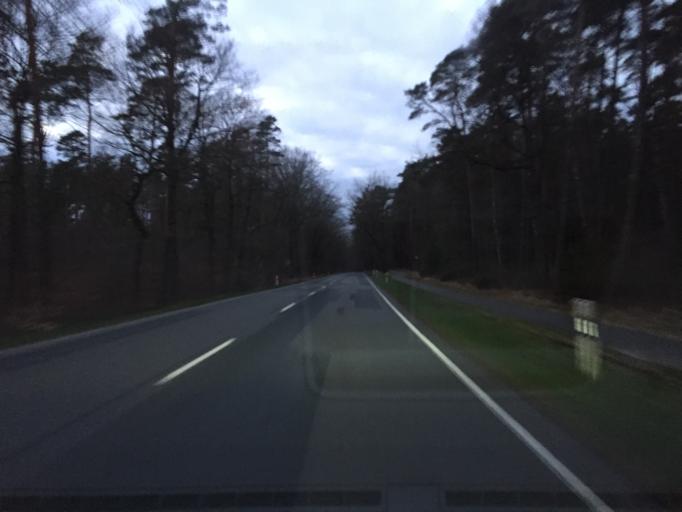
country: DE
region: Lower Saxony
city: Stockse
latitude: 52.6599
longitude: 9.3169
